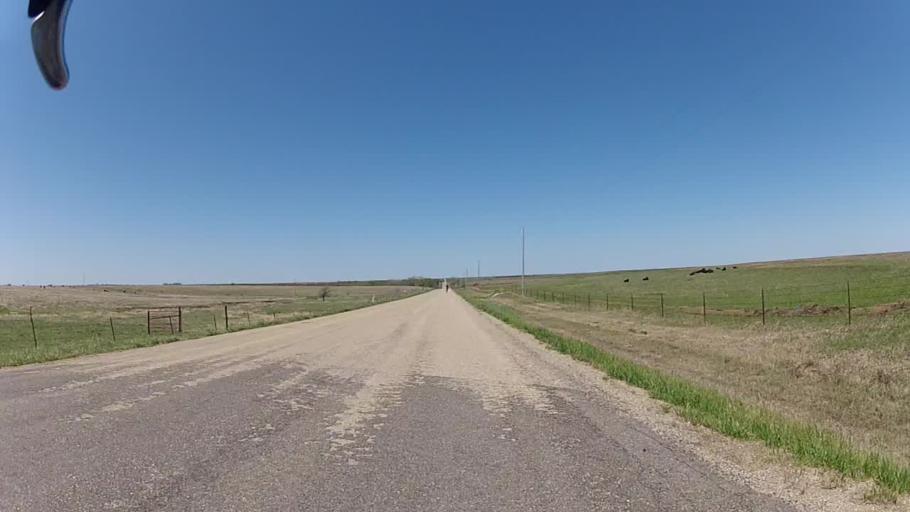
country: US
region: Kansas
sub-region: Riley County
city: Manhattan
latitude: 38.9716
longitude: -96.5358
